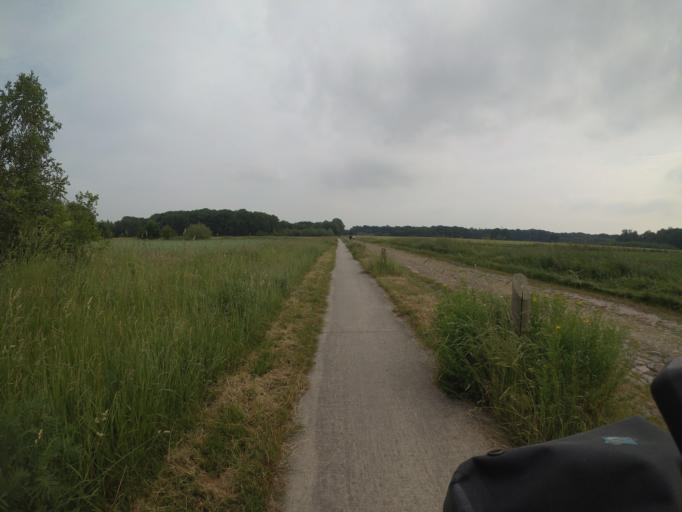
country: NL
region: Drenthe
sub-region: Gemeente Emmen
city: Emmen
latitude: 52.8355
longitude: 6.8869
